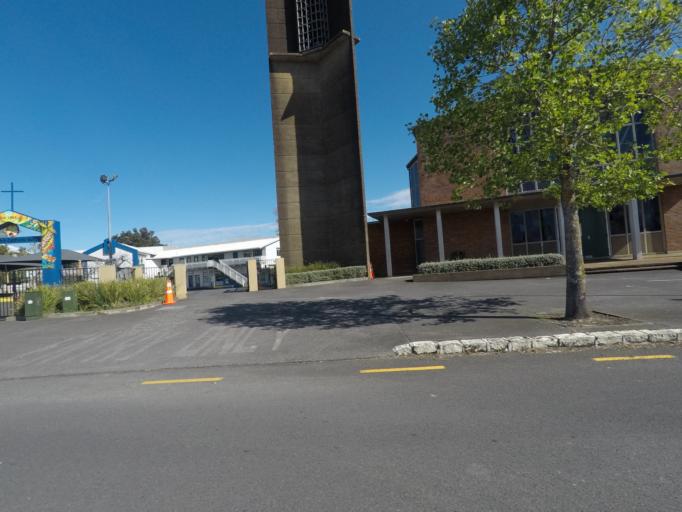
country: NZ
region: Auckland
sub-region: Auckland
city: Auckland
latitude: -36.8670
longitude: 174.7395
